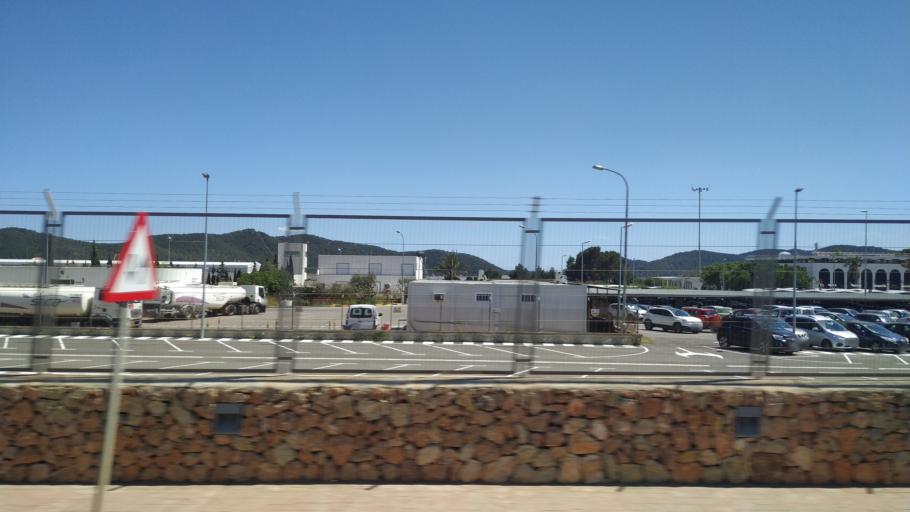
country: ES
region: Balearic Islands
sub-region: Illes Balears
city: Ibiza
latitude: 38.8805
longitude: 1.3732
